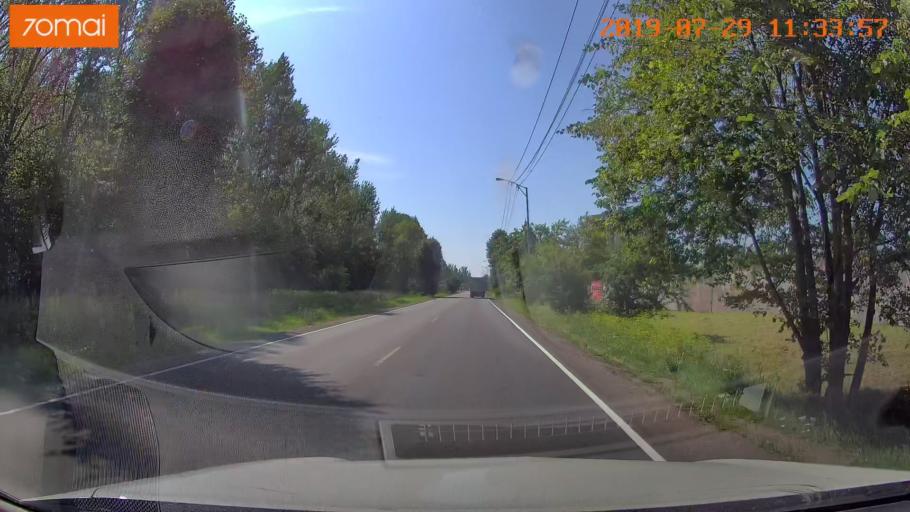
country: RU
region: Kaliningrad
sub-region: Gorod Kaliningrad
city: Kaliningrad
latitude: 54.6599
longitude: 20.5412
